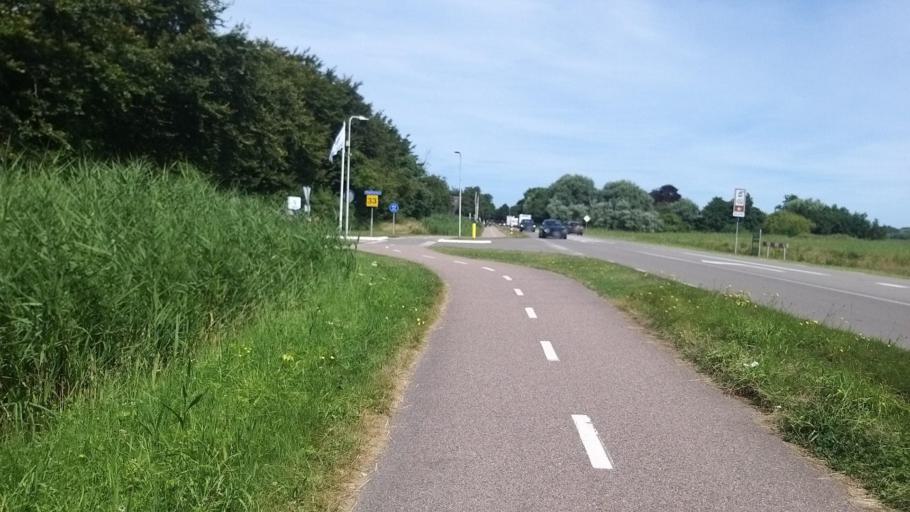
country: NL
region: North Holland
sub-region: Gemeente Texel
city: Den Burg
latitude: 53.1486
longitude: 4.8623
